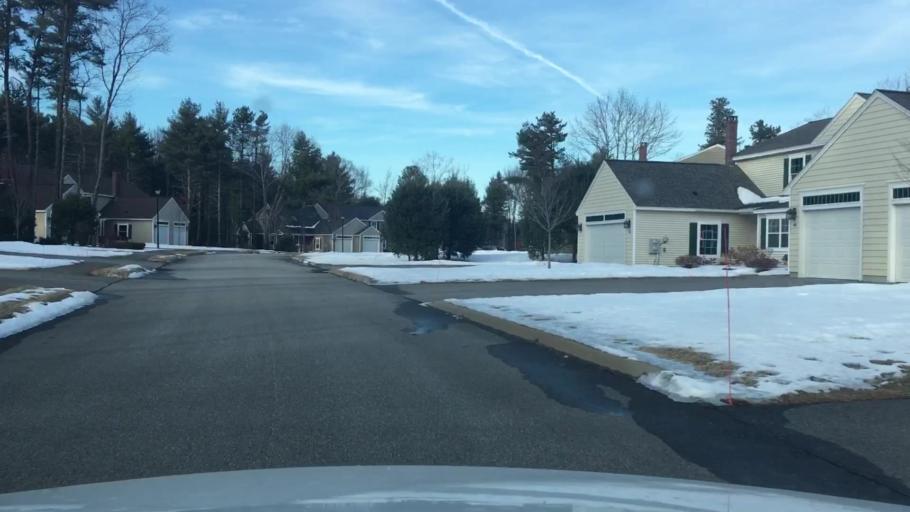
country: US
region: Maine
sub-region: York County
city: Wells Beach Station
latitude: 43.3522
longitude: -70.5681
